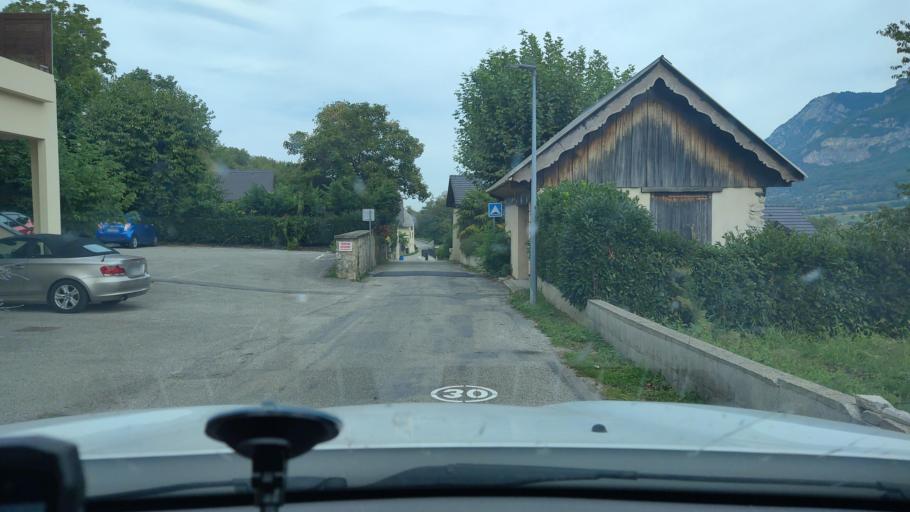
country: FR
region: Rhone-Alpes
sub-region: Departement de la Savoie
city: Voglans
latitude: 45.6293
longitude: 5.9092
